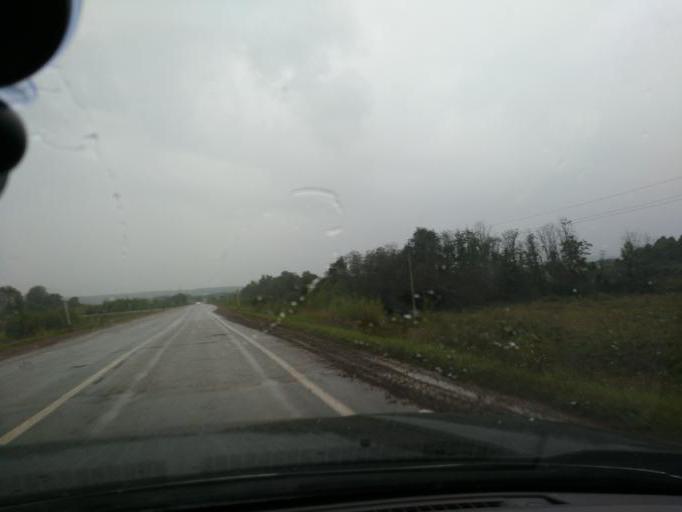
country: RU
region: Perm
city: Barda
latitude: 56.9441
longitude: 55.6188
